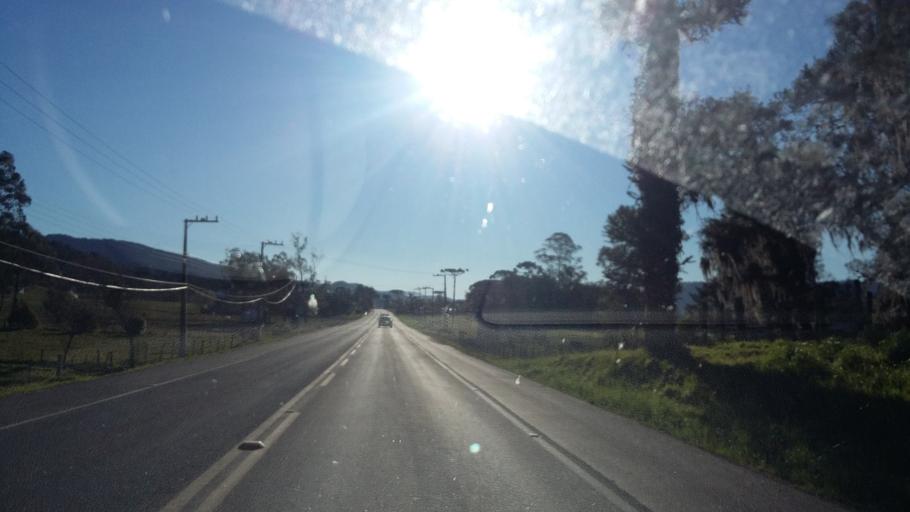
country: BR
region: Santa Catarina
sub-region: Lauro Muller
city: Lauro Muller
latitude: -27.9953
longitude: -49.5652
